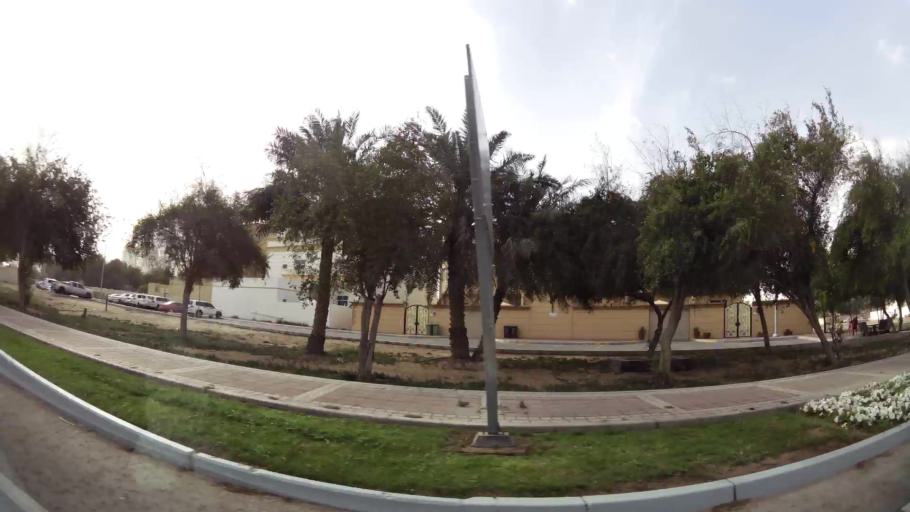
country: AE
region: Abu Dhabi
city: Abu Dhabi
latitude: 24.4163
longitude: 54.4696
